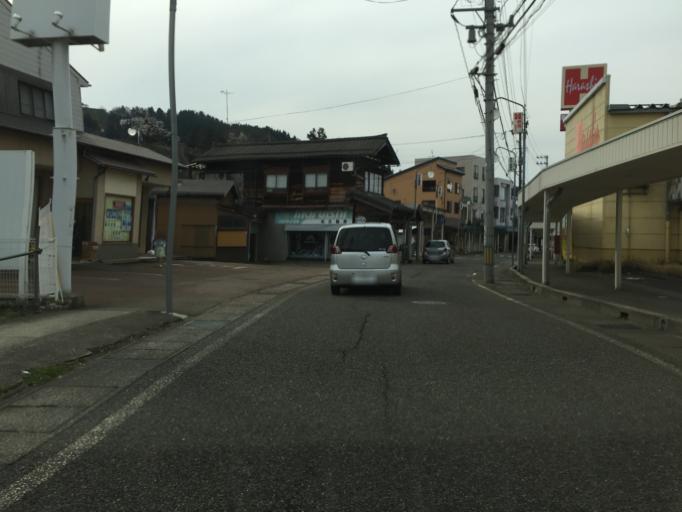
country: JP
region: Niigata
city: Tochio-honcho
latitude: 37.4729
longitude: 138.9979
